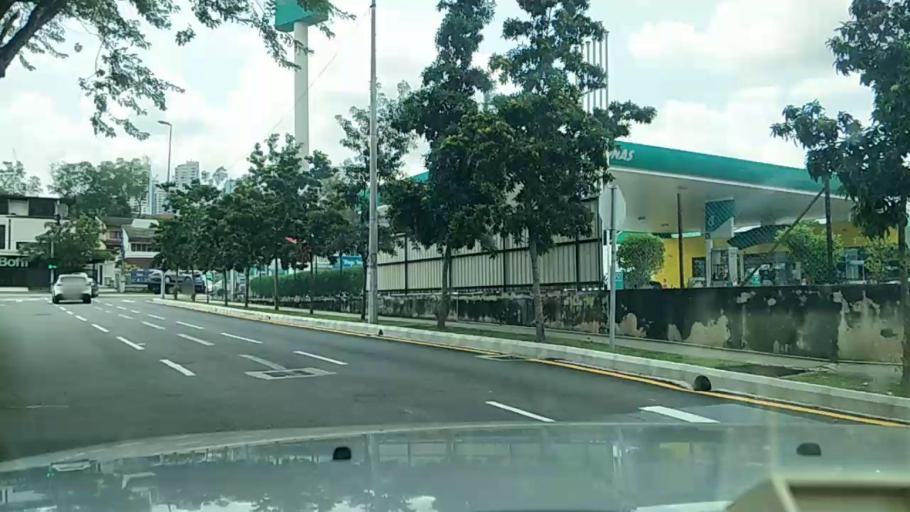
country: MY
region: Kuala Lumpur
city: Kuala Lumpur
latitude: 3.1370
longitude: 101.6733
